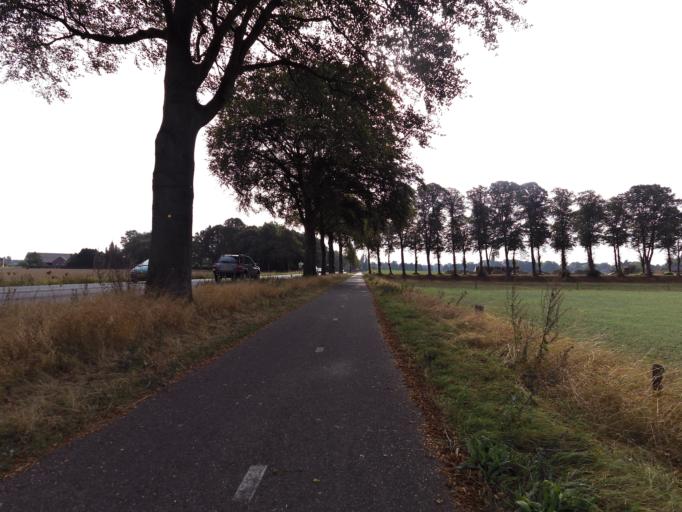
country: NL
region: Gelderland
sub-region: Oude IJsselstreek
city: Gendringen
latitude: 51.8975
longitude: 6.3905
